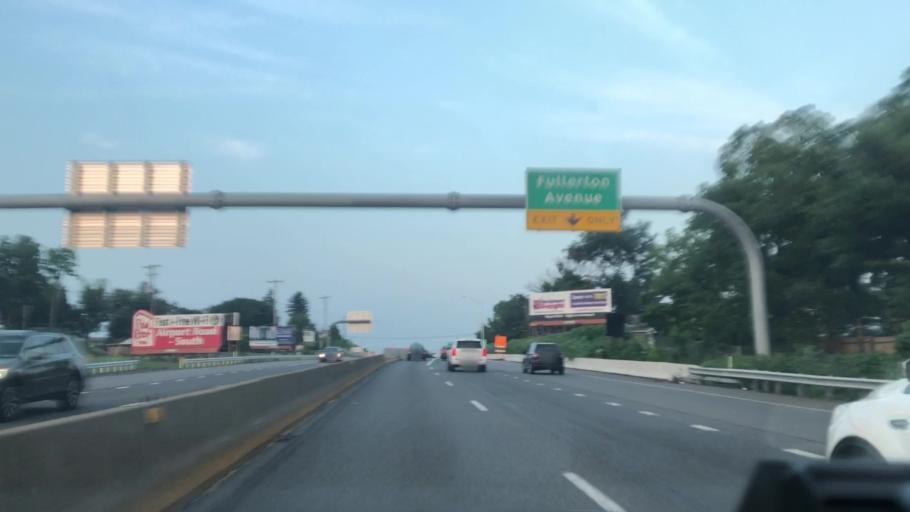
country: US
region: Pennsylvania
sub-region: Lehigh County
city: Fullerton
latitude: 40.6284
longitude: -75.4767
